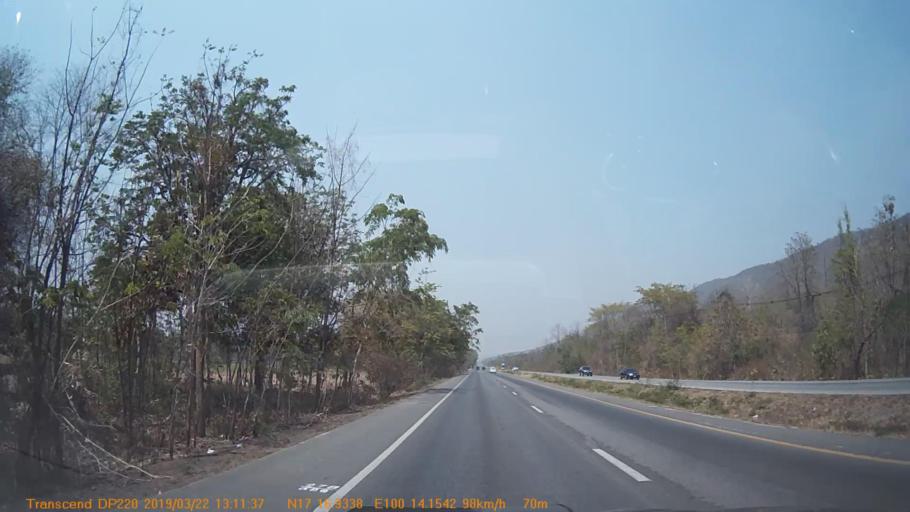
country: TH
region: Uttaradit
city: Phichai
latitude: 17.2827
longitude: 100.2358
